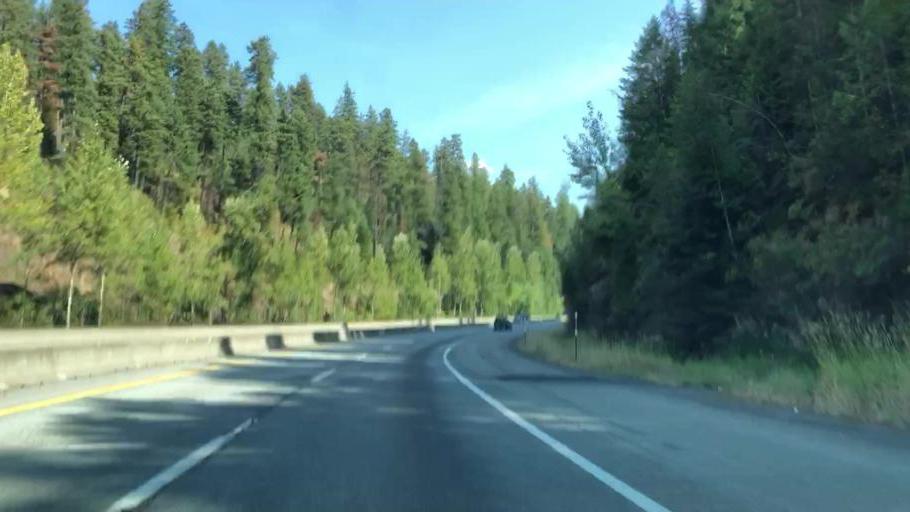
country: US
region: Idaho
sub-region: Kootenai County
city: Coeur d'Alene
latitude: 47.6242
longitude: -116.5636
